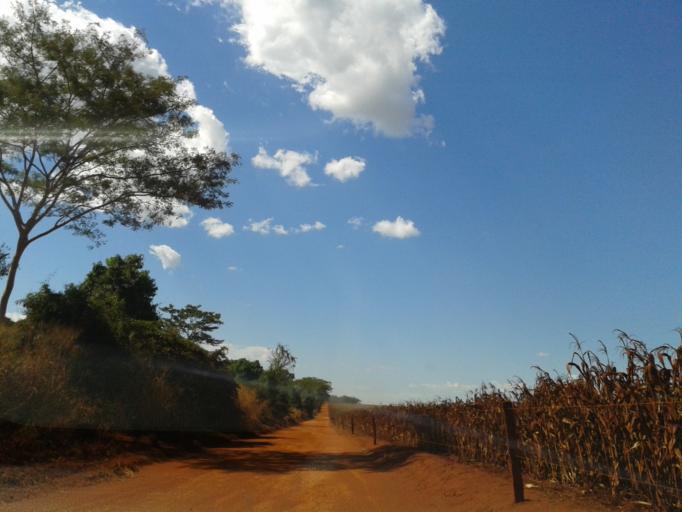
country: BR
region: Minas Gerais
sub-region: Capinopolis
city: Capinopolis
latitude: -18.6202
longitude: -49.4854
